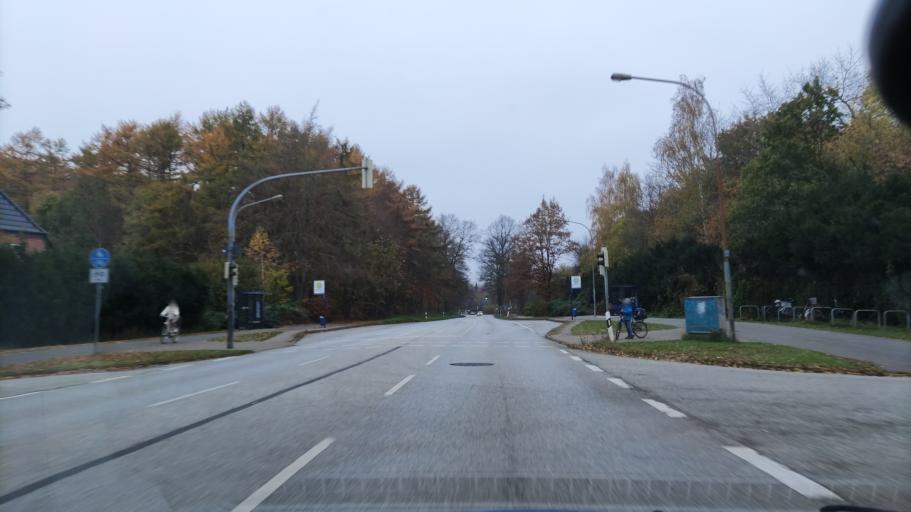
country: DE
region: Schleswig-Holstein
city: Gross Gronau
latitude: 53.8308
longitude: 10.7177
